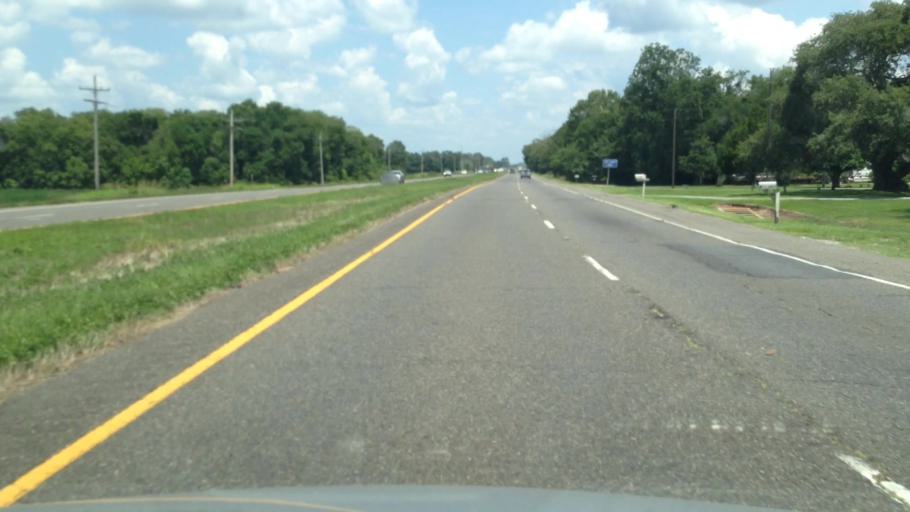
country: US
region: Louisiana
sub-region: Saint Landry Parish
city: Port Barre
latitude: 30.5478
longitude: -91.9852
